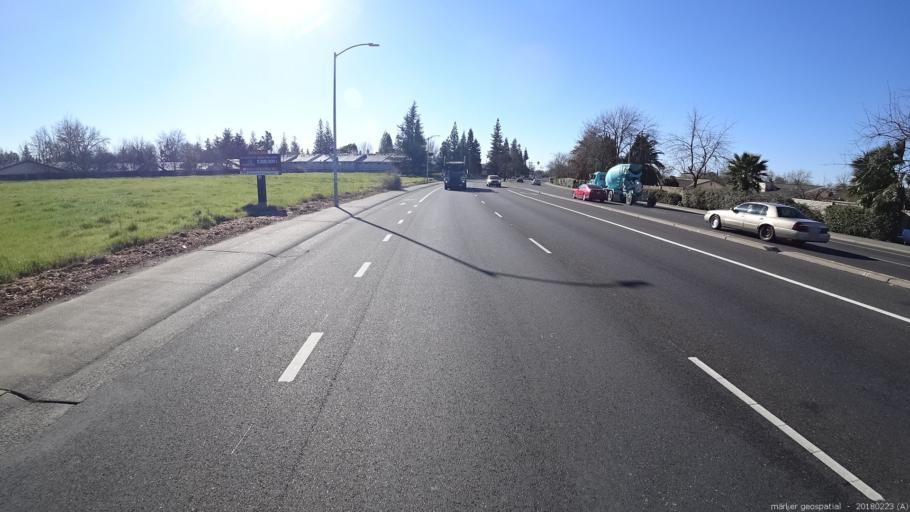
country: US
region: California
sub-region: Sacramento County
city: North Highlands
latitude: 38.7072
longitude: -121.3832
